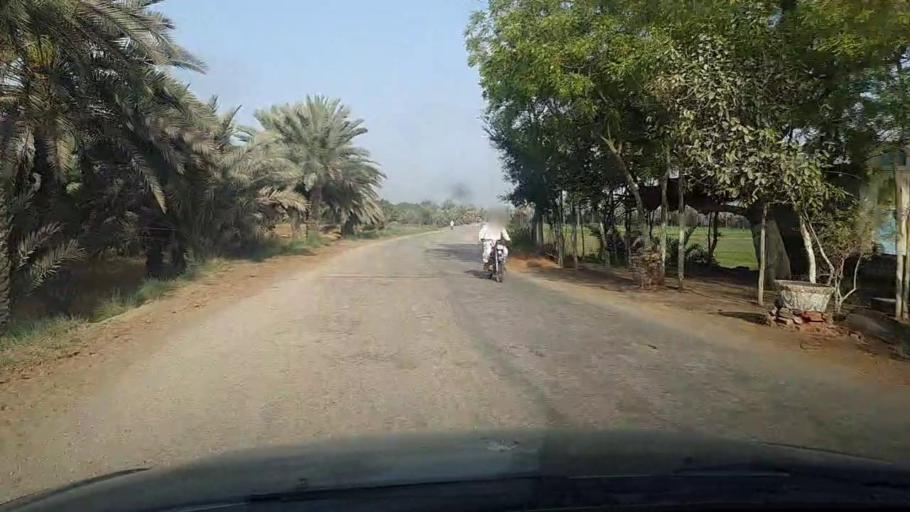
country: PK
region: Sindh
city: Pir jo Goth
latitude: 27.5631
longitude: 68.6562
